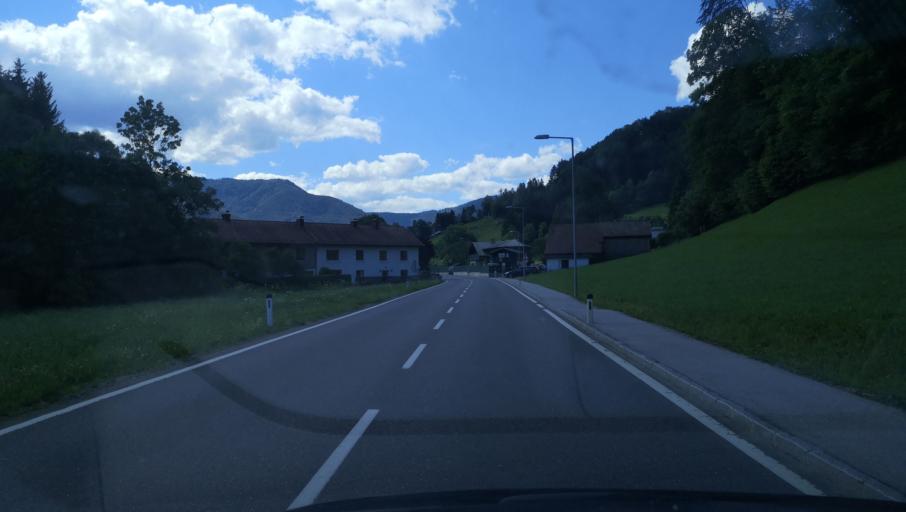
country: AT
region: Lower Austria
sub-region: Politischer Bezirk Scheibbs
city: Gresten
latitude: 47.9643
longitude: 15.0237
